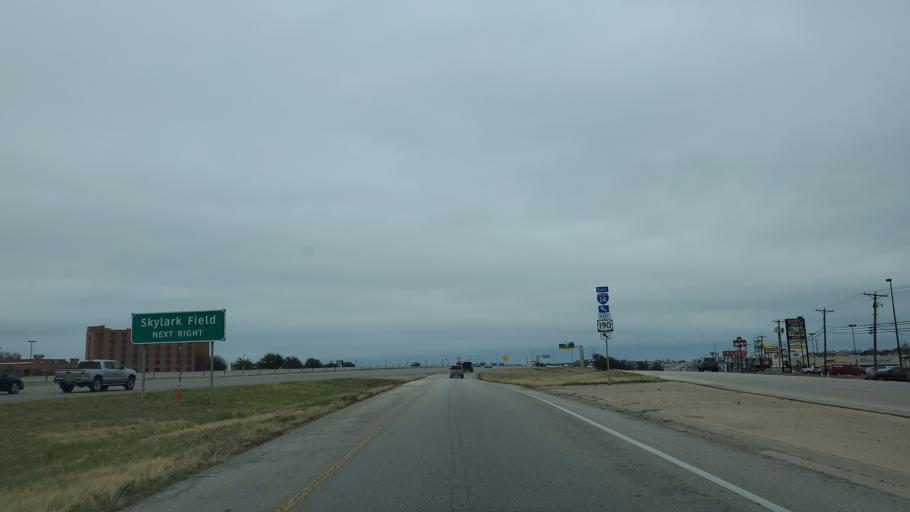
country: US
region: Texas
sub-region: Bell County
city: Killeen
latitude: 31.0923
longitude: -97.7245
